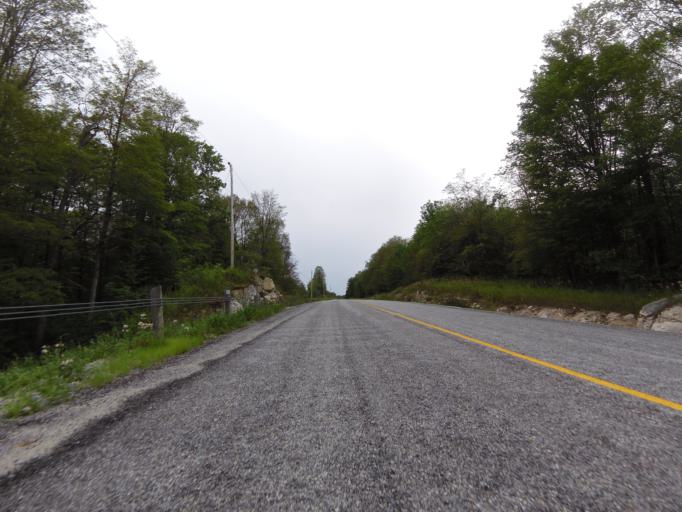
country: CA
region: Ontario
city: Perth
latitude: 44.8992
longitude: -76.4959
